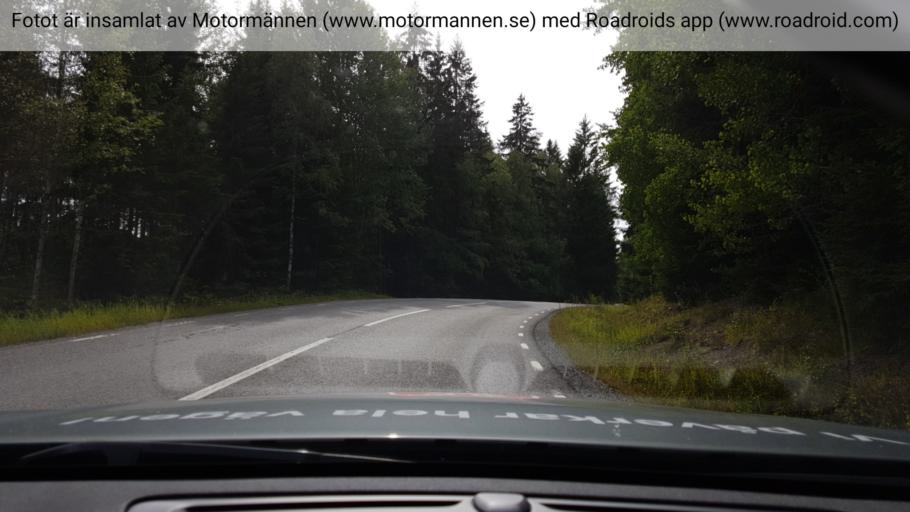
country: SE
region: Stockholm
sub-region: Botkyrka Kommun
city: Tullinge
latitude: 59.1320
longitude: 17.9589
